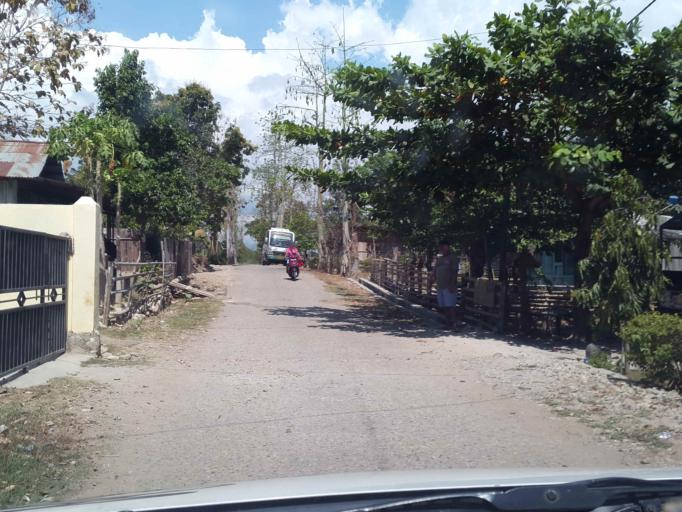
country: ID
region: East Nusa Tenggara
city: Atambua
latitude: -9.0834
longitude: 124.9001
